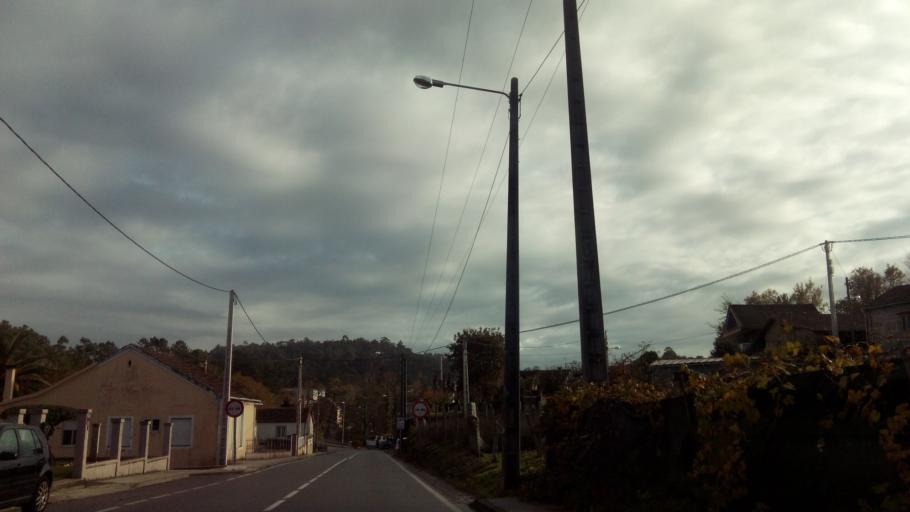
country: ES
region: Galicia
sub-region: Provincia de Pontevedra
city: Ponteareas
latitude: 42.1613
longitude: -8.5062
